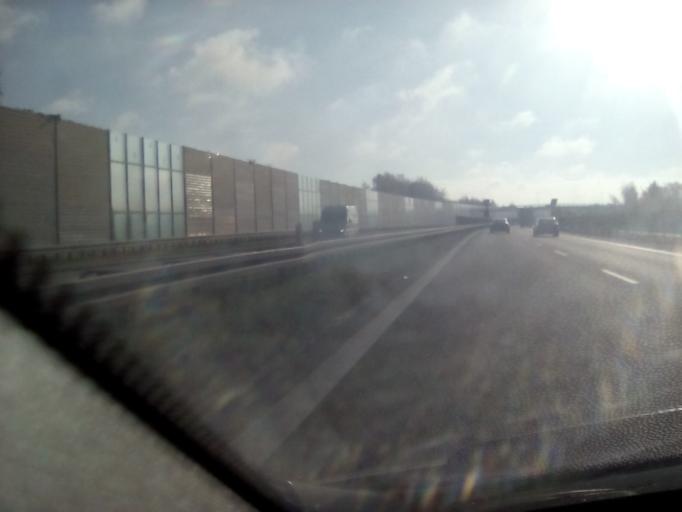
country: PL
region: Masovian Voivodeship
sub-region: Powiat grojecki
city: Grojec
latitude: 51.8572
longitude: 20.8616
